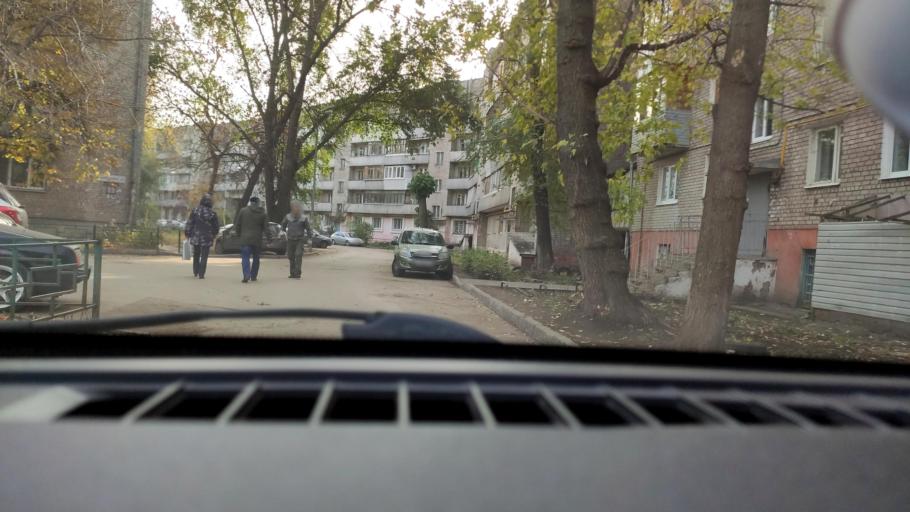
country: RU
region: Samara
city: Samara
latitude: 53.2165
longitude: 50.2705
